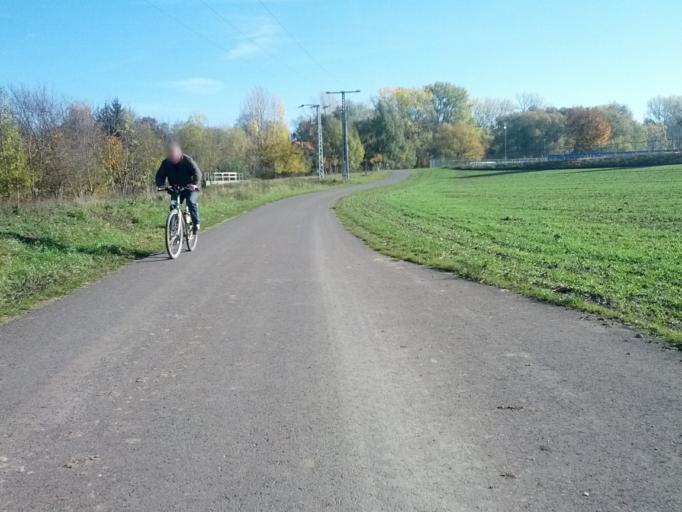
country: DE
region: Thuringia
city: Remstadt
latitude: 50.9686
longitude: 10.6969
